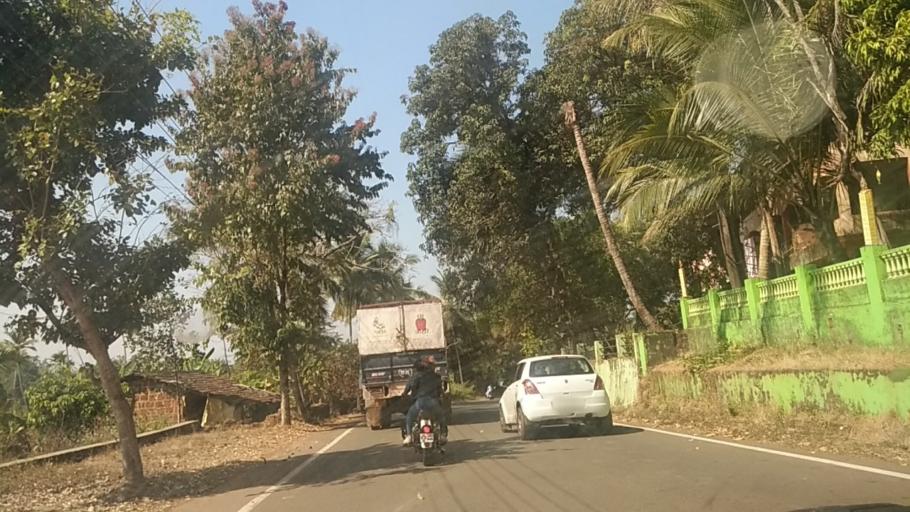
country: IN
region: Goa
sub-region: South Goa
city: Curchorem
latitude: 15.3003
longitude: 74.0660
